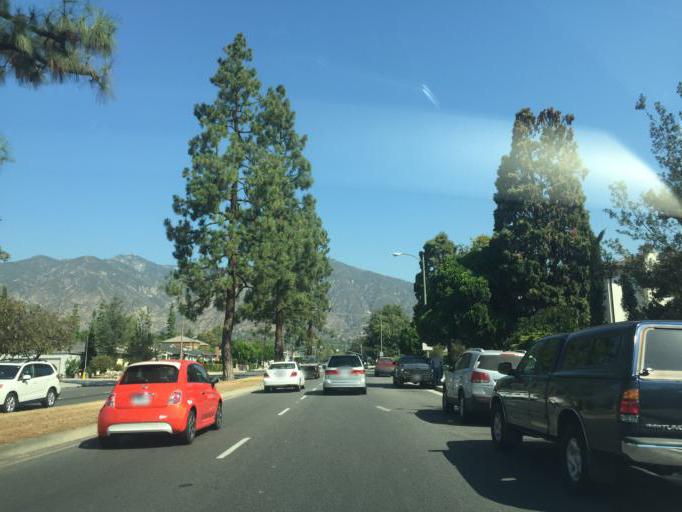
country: US
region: California
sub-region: Los Angeles County
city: Arcadia
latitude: 34.1488
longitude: -118.0316
